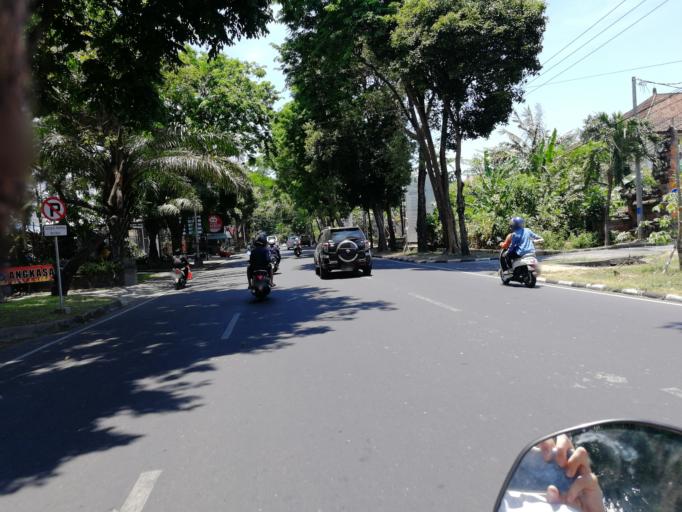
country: ID
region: Bali
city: Denpasar
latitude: -8.6670
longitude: 115.2261
